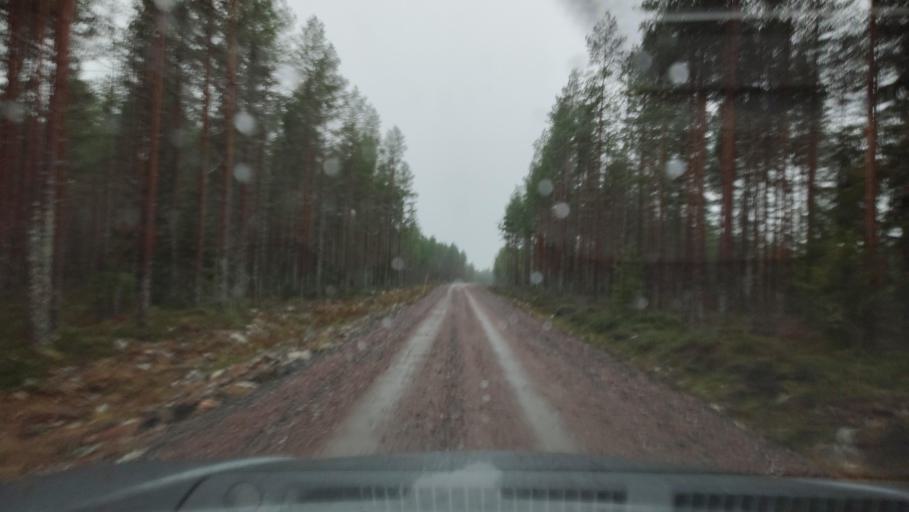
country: FI
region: Southern Ostrobothnia
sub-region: Suupohja
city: Karijoki
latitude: 62.1758
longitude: 21.7114
